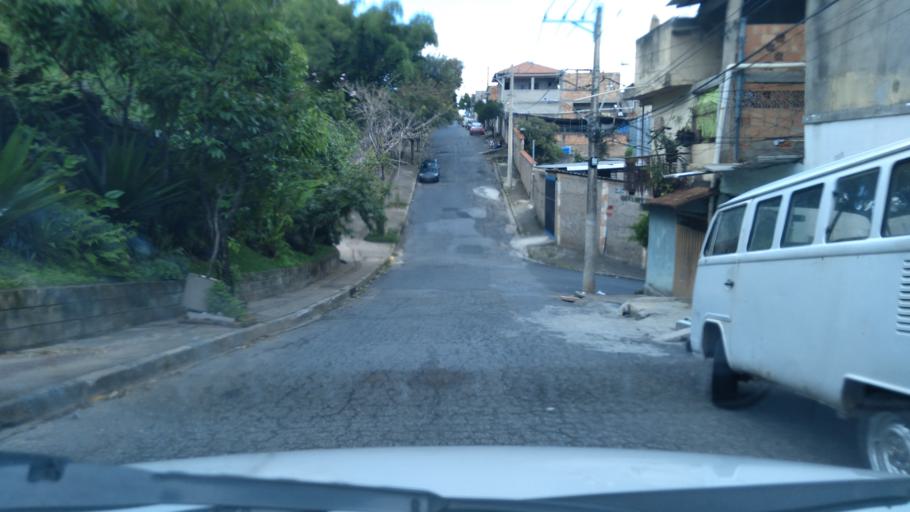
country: BR
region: Minas Gerais
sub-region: Belo Horizonte
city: Belo Horizonte
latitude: -19.9161
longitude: -43.8954
